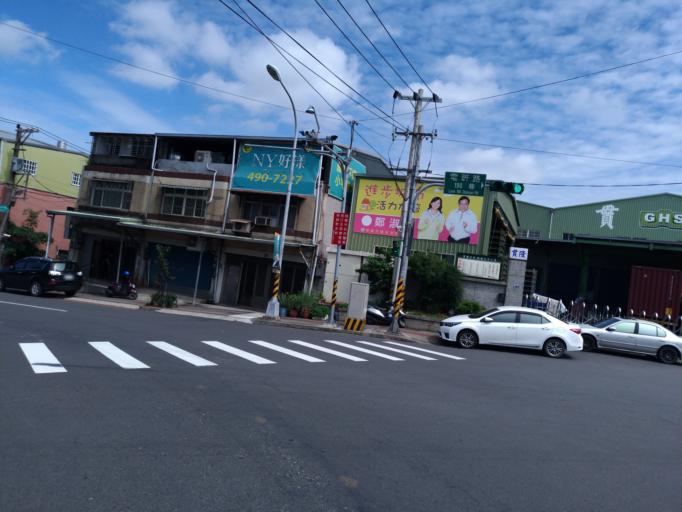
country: TW
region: Taiwan
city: Taoyuan City
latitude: 24.9555
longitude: 121.1679
